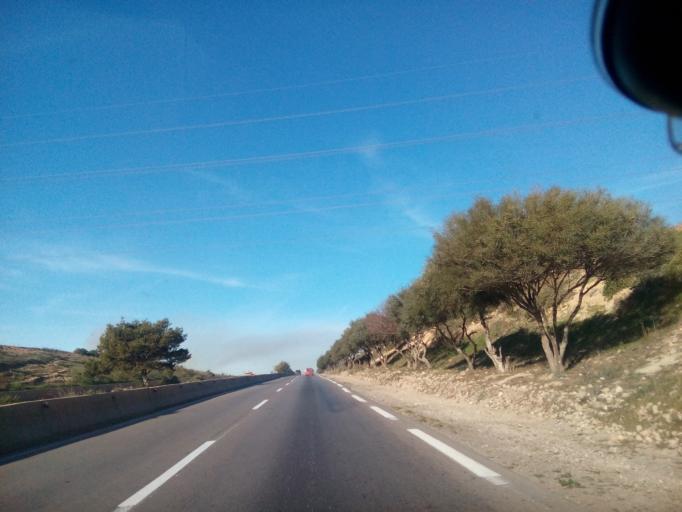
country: DZ
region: Oran
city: Ain el Bya
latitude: 35.7716
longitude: -0.2427
